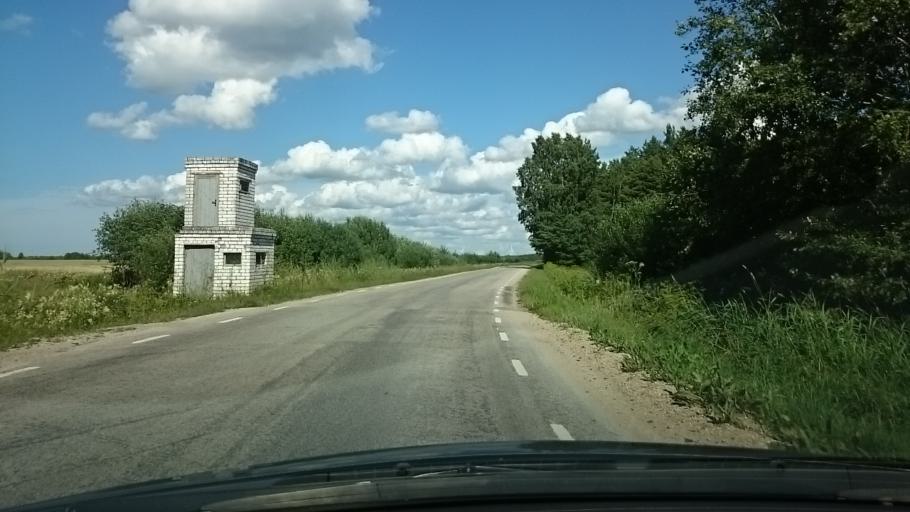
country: EE
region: Laeaene
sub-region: Haapsalu linn
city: Haapsalu
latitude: 59.0466
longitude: 23.5095
